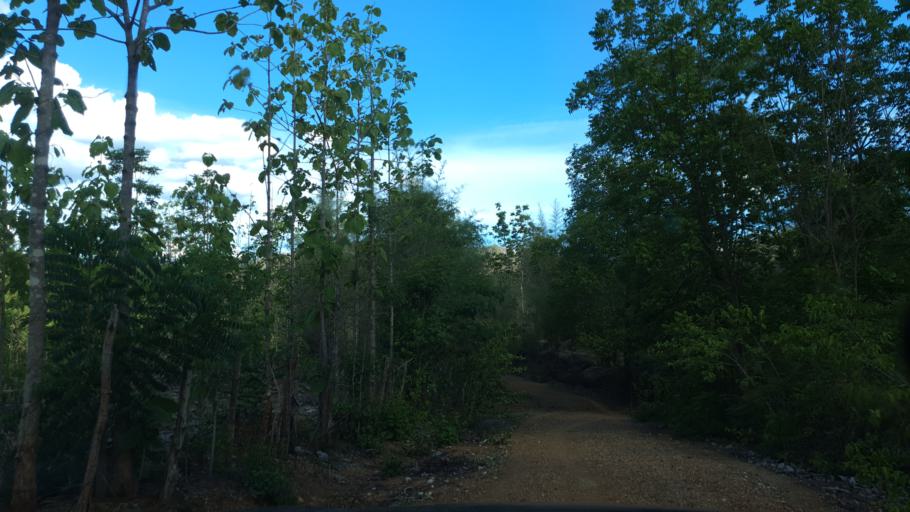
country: TH
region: Lampang
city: Sop Prap
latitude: 17.8530
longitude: 99.2835
